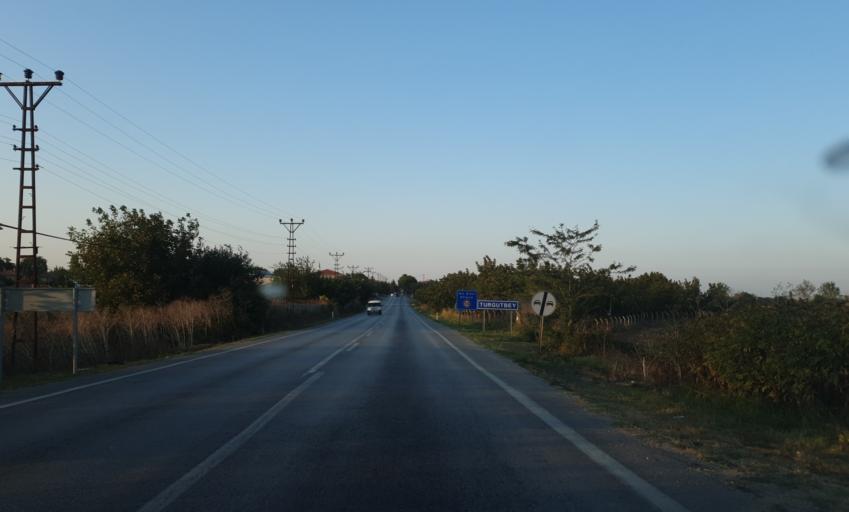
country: TR
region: Kirklareli
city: Luleburgaz
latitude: 41.4539
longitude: 27.3855
